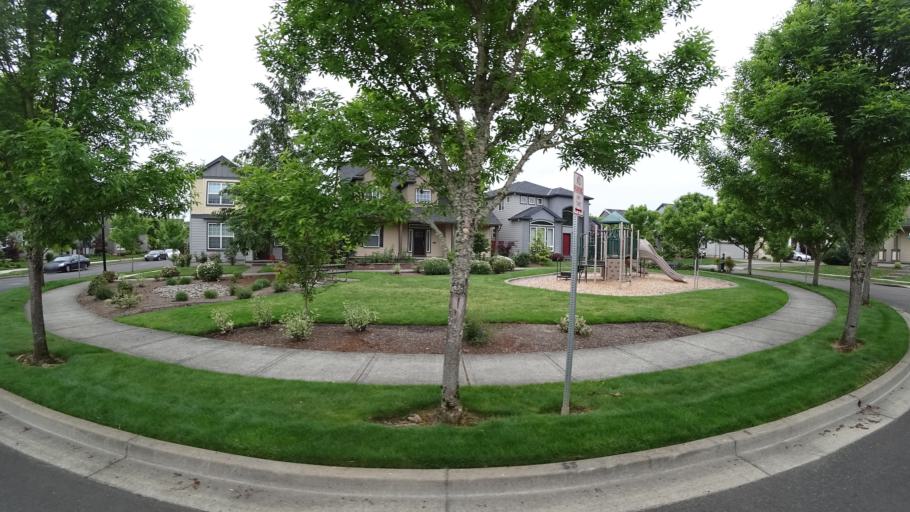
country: US
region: Oregon
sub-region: Washington County
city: Aloha
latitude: 45.4948
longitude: -122.9193
